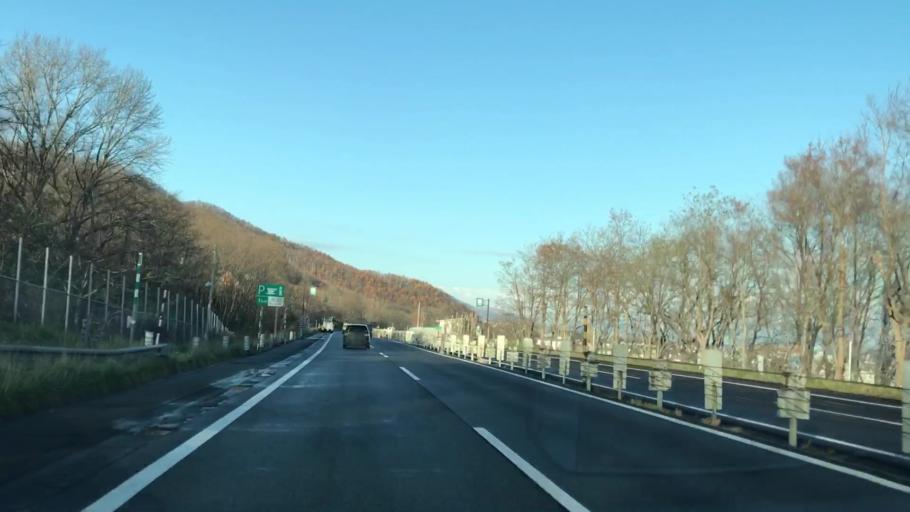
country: JP
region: Hokkaido
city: Sapporo
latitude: 43.1185
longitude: 141.2266
